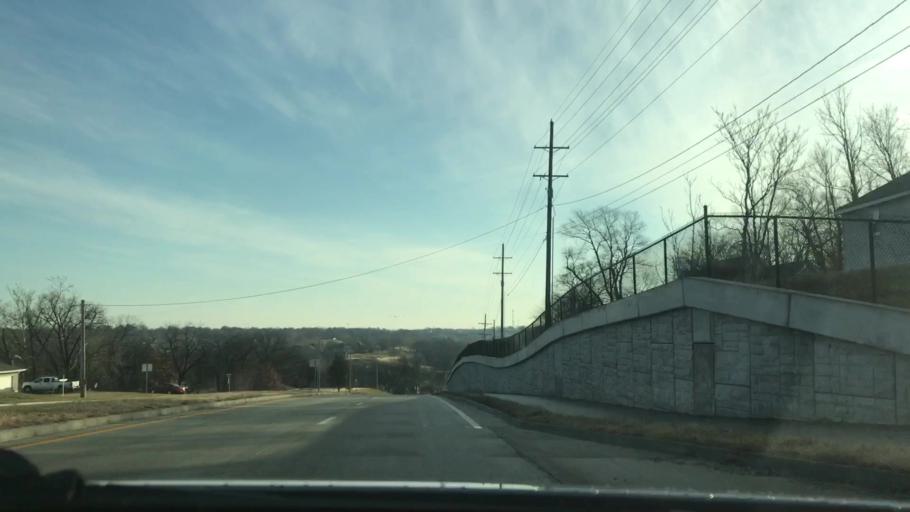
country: US
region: Missouri
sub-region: Platte County
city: Weatherby Lake
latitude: 39.2118
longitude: -94.7214
